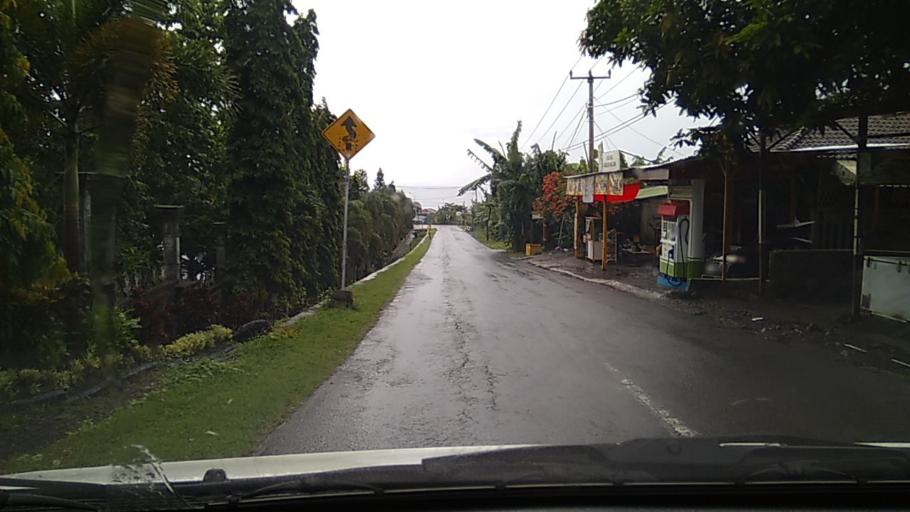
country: ID
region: Bali
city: Banjar Danginsema
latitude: -8.4661
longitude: 115.6304
